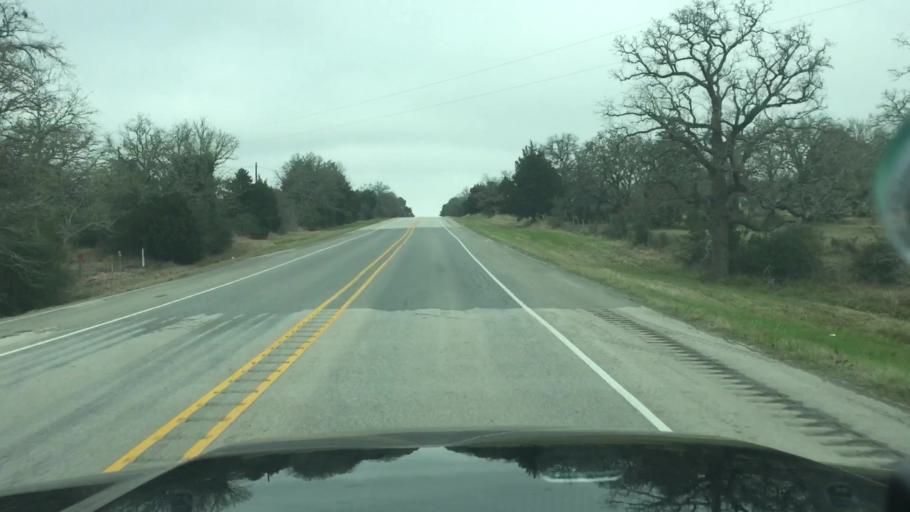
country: US
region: Texas
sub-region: Lee County
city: Giddings
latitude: 30.0743
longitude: -96.9169
